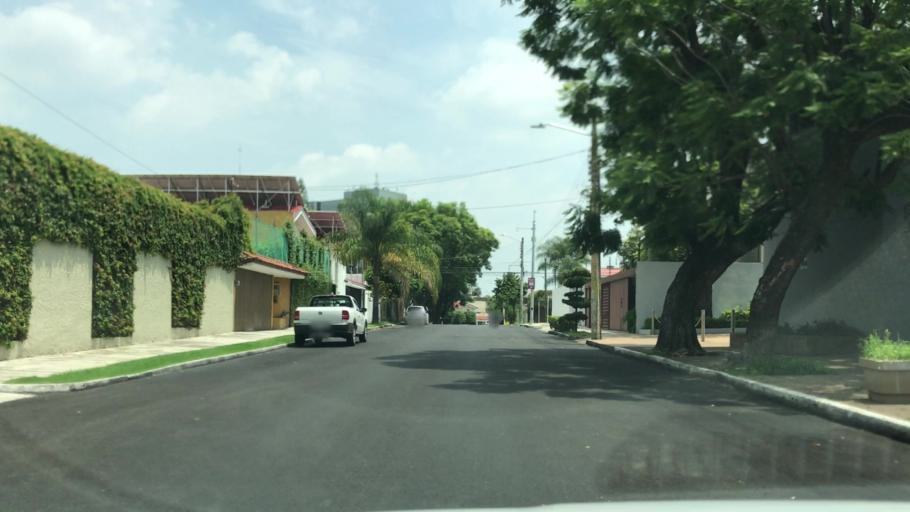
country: MX
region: Jalisco
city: Guadalajara
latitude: 20.6537
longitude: -103.4048
